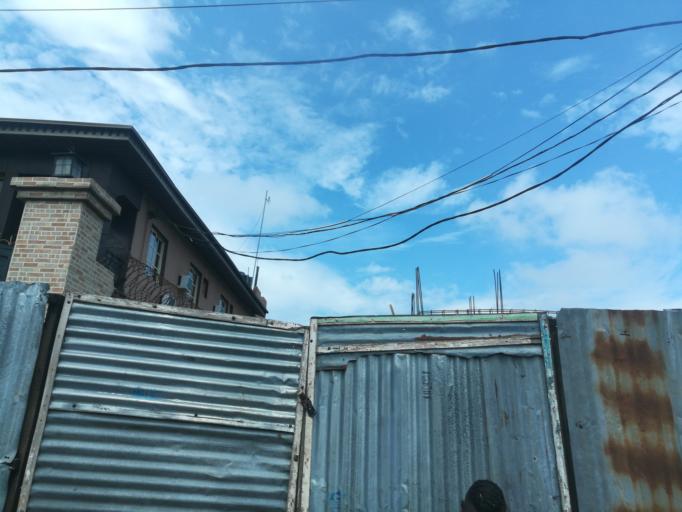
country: NG
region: Lagos
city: Agege
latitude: 6.6220
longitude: 3.3308
